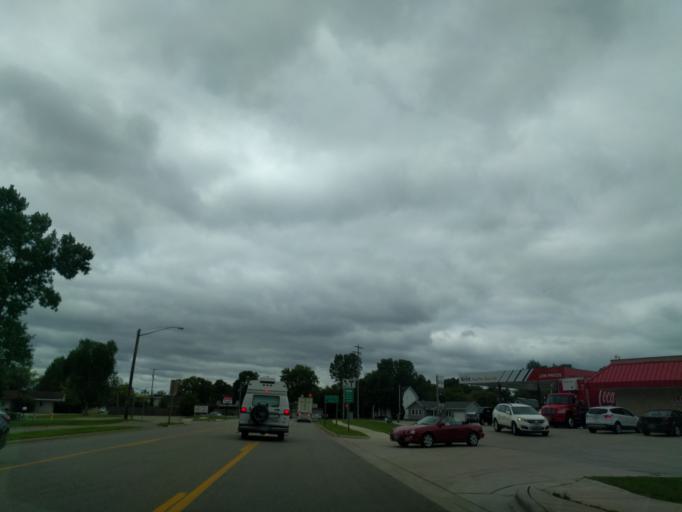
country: US
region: Michigan
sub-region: Menominee County
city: Menominee
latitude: 45.1352
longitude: -87.6112
